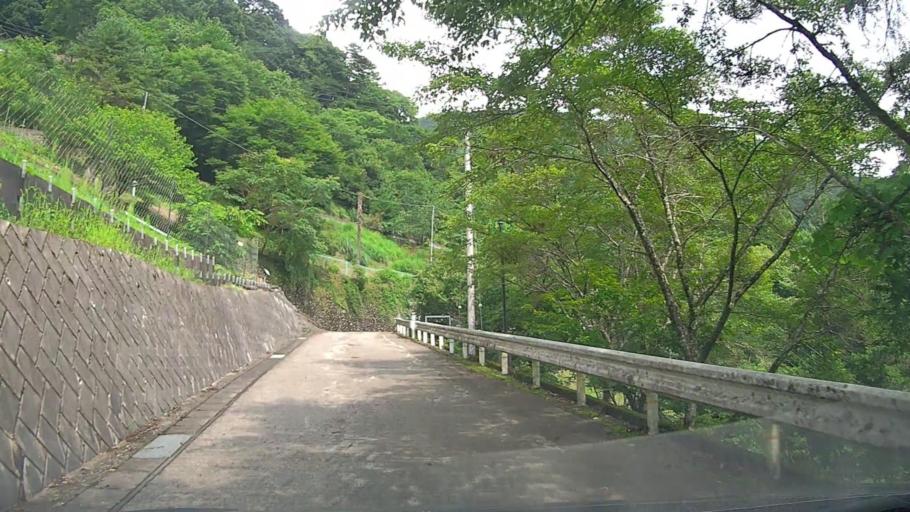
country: JP
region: Yamanashi
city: Uenohara
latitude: 35.7501
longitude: 139.0811
